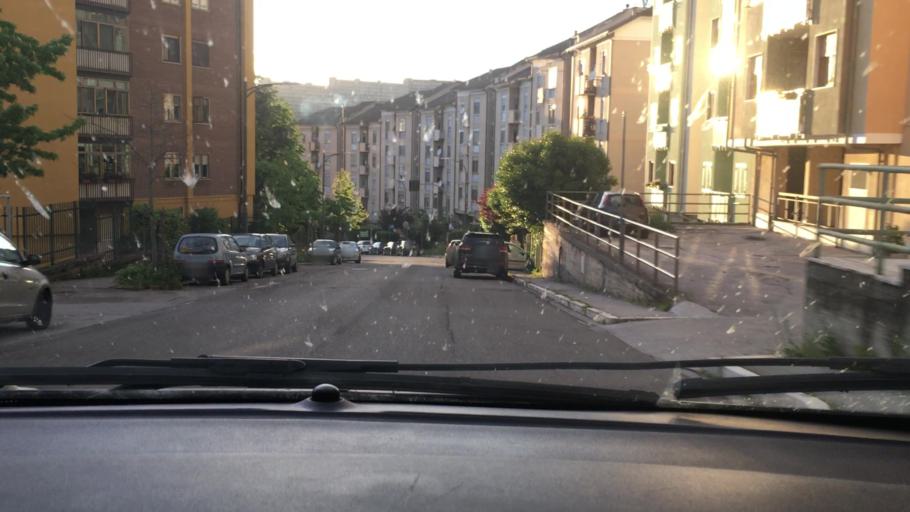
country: IT
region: Basilicate
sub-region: Provincia di Potenza
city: Potenza
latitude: 40.6291
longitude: 15.7998
